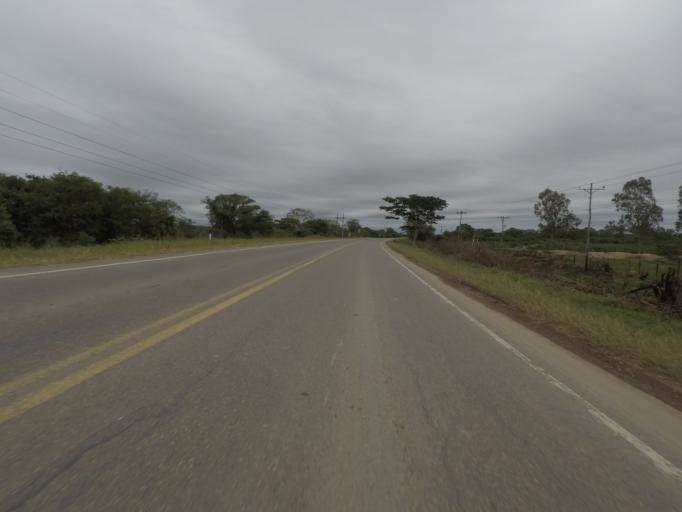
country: BO
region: Santa Cruz
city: Pailon
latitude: -17.6625
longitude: -62.7334
